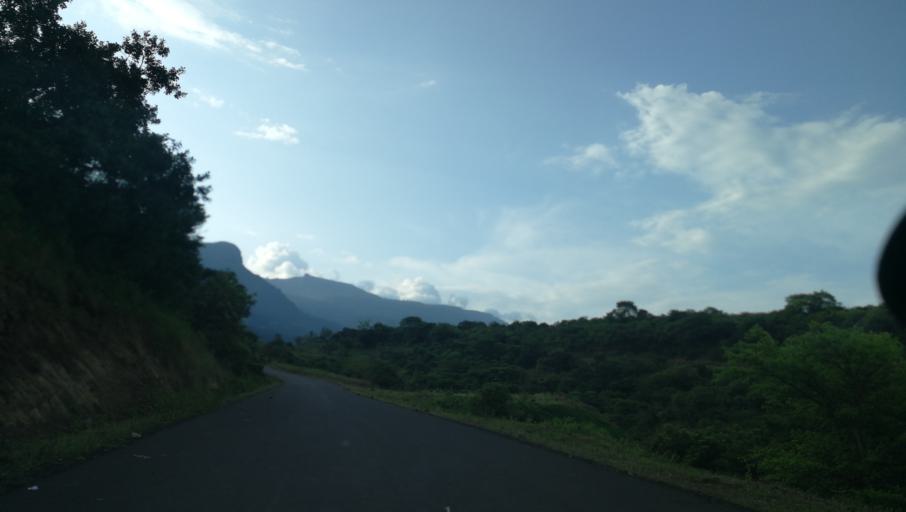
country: ET
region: Southern Nations, Nationalities, and People's Region
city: Areka
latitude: 6.8476
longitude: 37.2759
